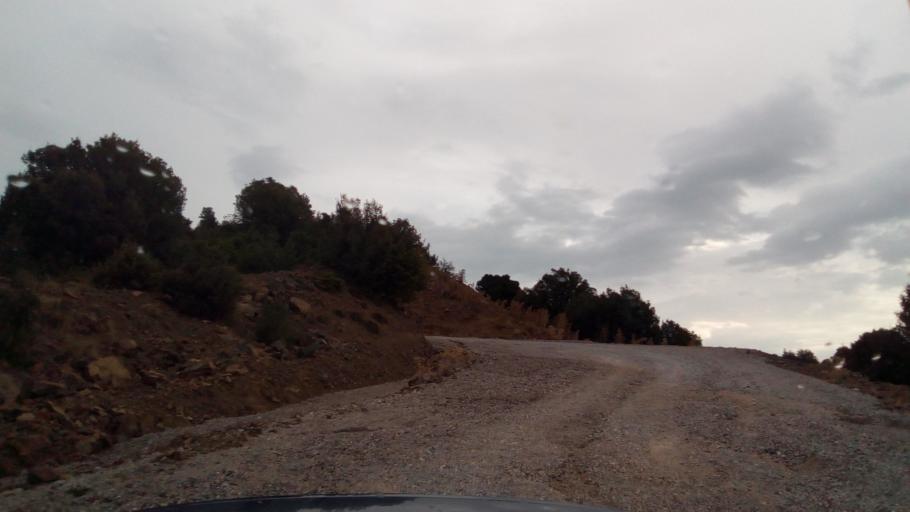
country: GR
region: Central Greece
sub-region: Nomos Fokidos
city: Lidoriki
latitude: 38.4462
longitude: 22.0718
